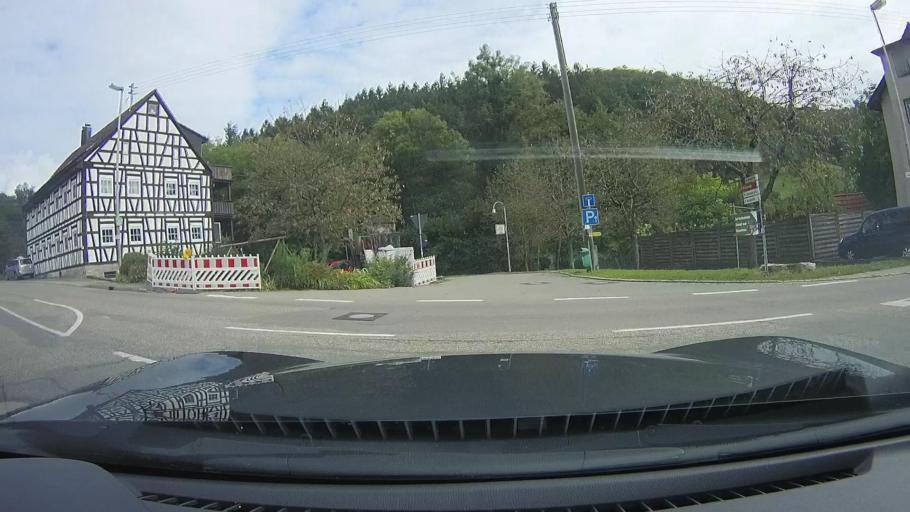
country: DE
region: Baden-Wuerttemberg
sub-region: Regierungsbezirk Stuttgart
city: Spiegelberg
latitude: 49.0396
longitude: 9.4458
